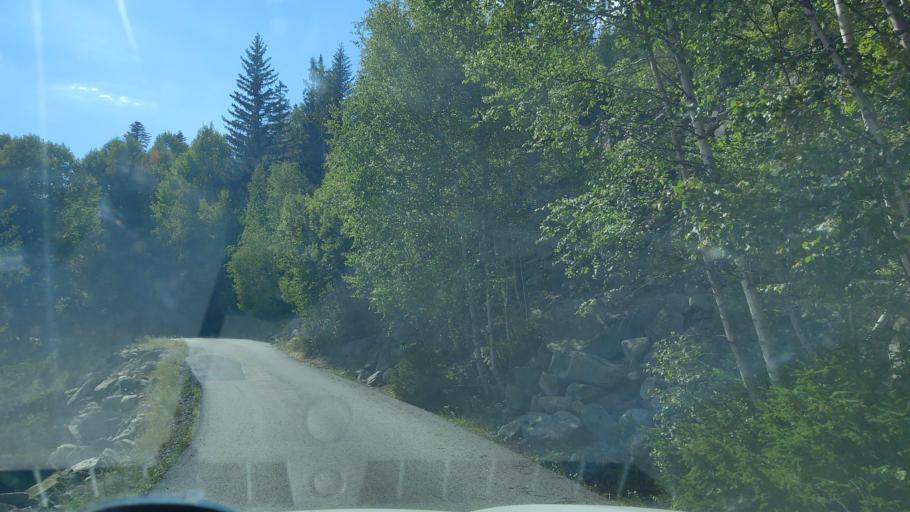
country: FR
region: Rhone-Alpes
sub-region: Departement de la Savoie
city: Val Thorens
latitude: 45.2211
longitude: 6.5615
